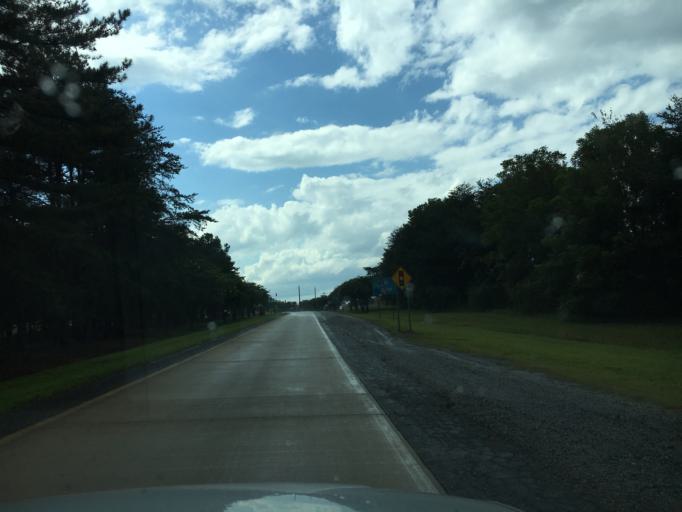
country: US
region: North Carolina
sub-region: Catawba County
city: Conover
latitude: 35.7035
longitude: -81.2600
